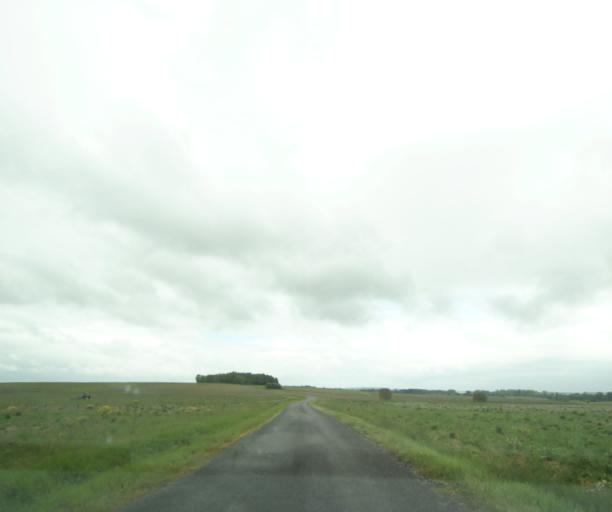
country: FR
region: Poitou-Charentes
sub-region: Departement de la Charente-Maritime
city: Perignac
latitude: 45.6688
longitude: -0.4975
